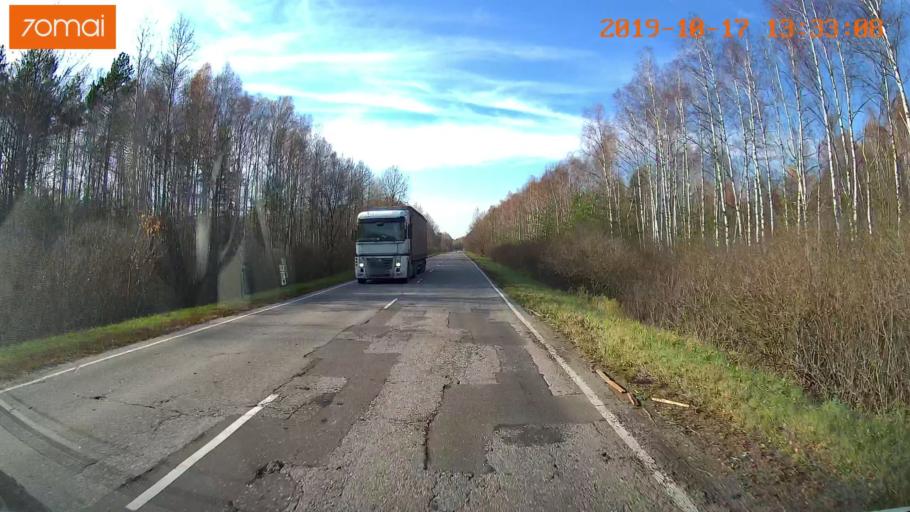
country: RU
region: Vladimir
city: Velikodvorskiy
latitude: 55.1409
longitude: 40.7485
